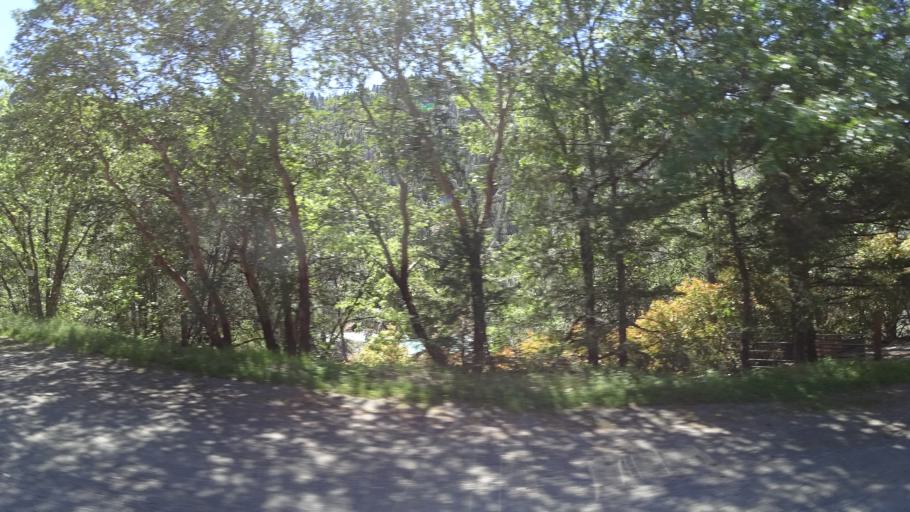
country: US
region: California
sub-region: Humboldt County
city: Willow Creek
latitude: 40.7869
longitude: -123.4271
